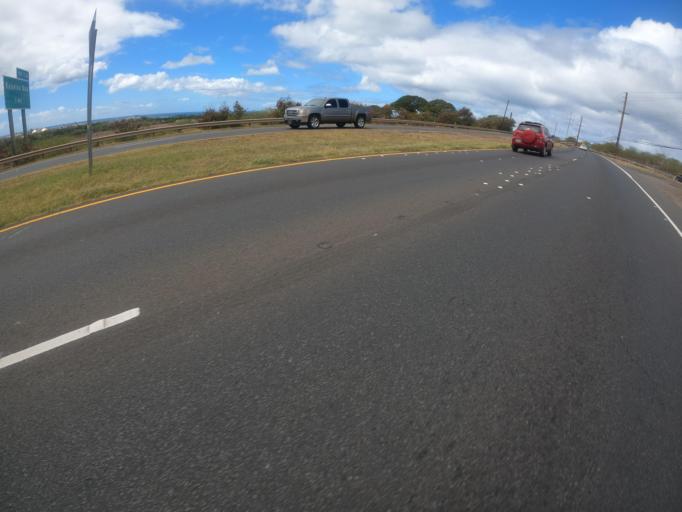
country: US
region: Hawaii
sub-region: Honolulu County
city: Makakilo City
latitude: 21.3410
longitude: -158.1037
